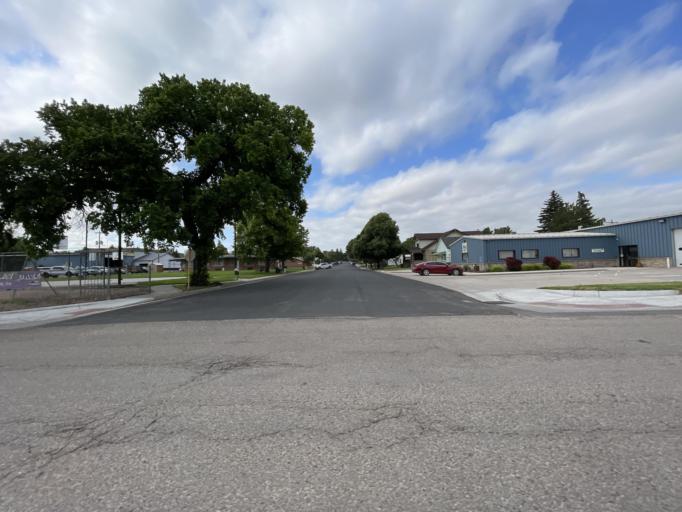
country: US
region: Colorado
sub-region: Yuma County
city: Wray
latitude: 40.0789
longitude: -102.2248
